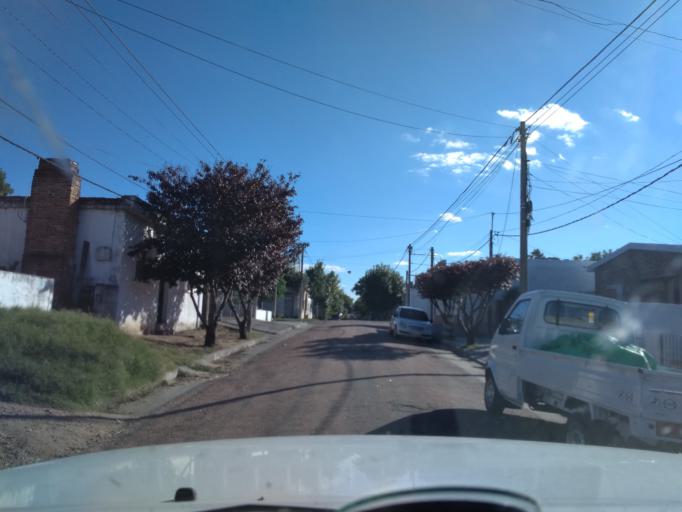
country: UY
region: Florida
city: Florida
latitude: -34.0941
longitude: -56.2091
